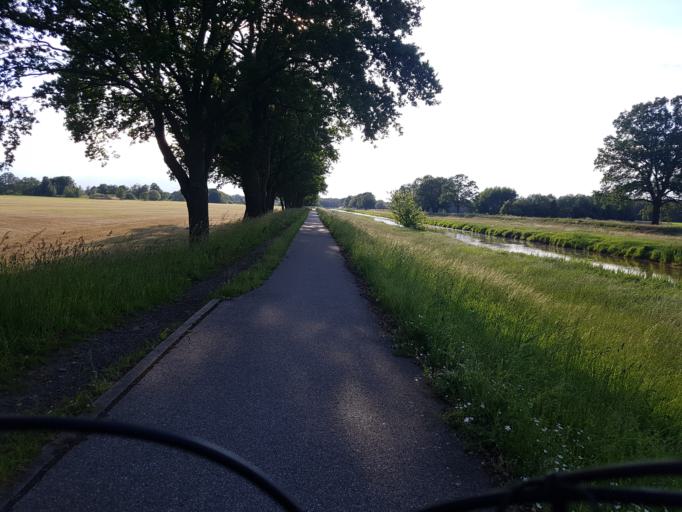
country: DE
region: Brandenburg
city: Elsterwerda
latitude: 51.4798
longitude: 13.4560
